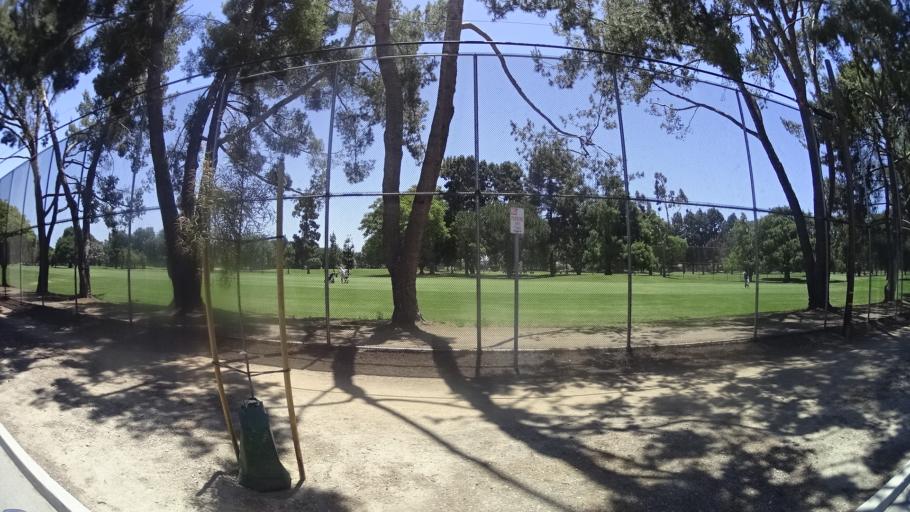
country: US
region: California
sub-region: Los Angeles County
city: Marina del Rey
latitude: 34.0062
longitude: -118.4633
